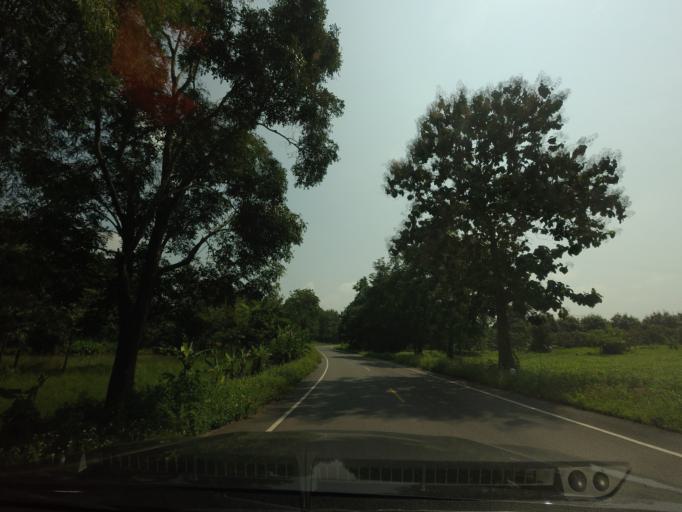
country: TH
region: Nan
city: Nan
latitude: 18.8551
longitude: 100.7894
